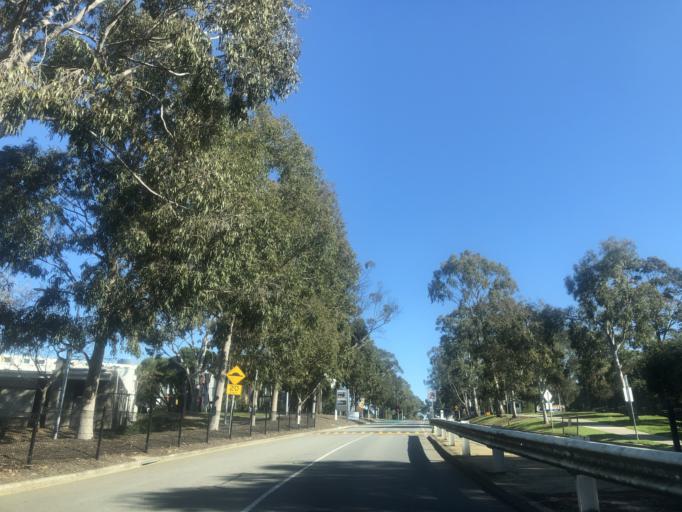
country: AU
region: Victoria
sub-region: Monash
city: Notting Hill
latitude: -37.9086
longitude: 145.1370
